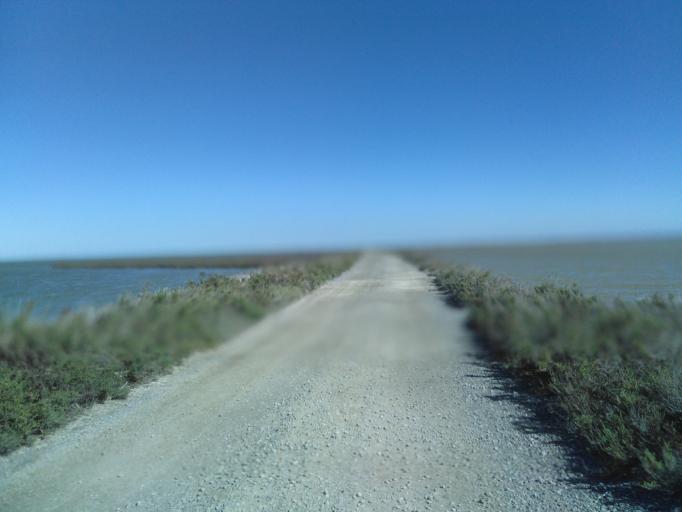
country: FR
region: Provence-Alpes-Cote d'Azur
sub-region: Departement des Bouches-du-Rhone
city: Saintes-Maries-de-la-Mer
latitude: 43.4240
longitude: 4.6188
